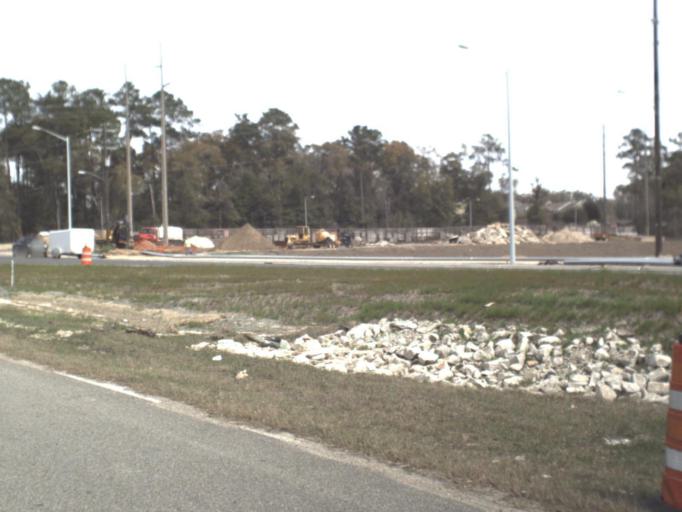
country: US
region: Florida
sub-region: Leon County
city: Tallahassee
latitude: 30.4298
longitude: -84.3528
